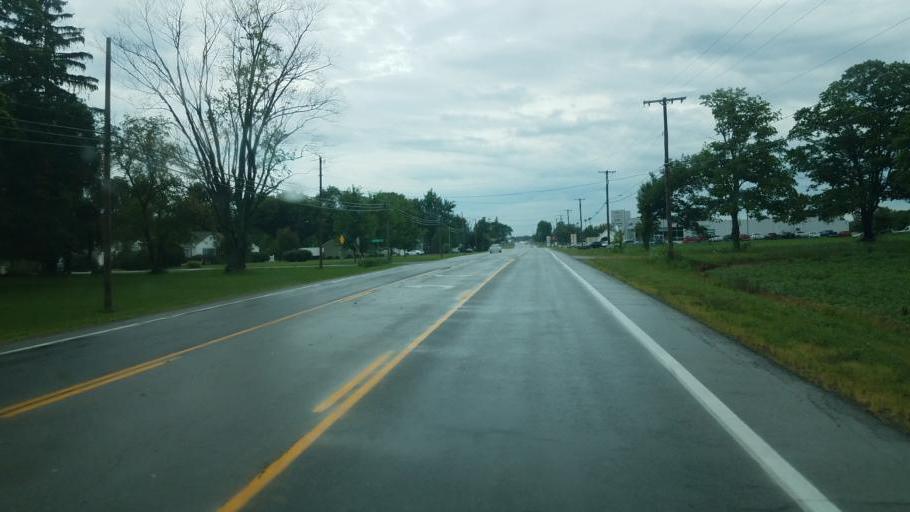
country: US
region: Ohio
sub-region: Marion County
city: Marion
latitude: 40.5514
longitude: -83.1147
